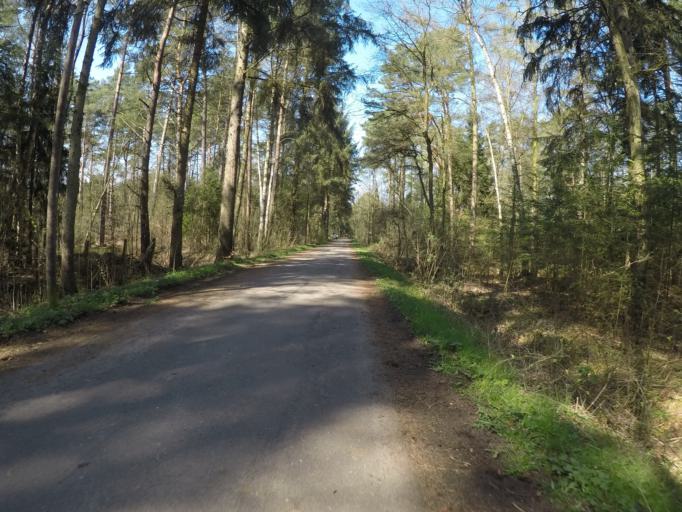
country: DE
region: Schleswig-Holstein
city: Pinneberg
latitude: 53.6185
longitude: 9.7767
